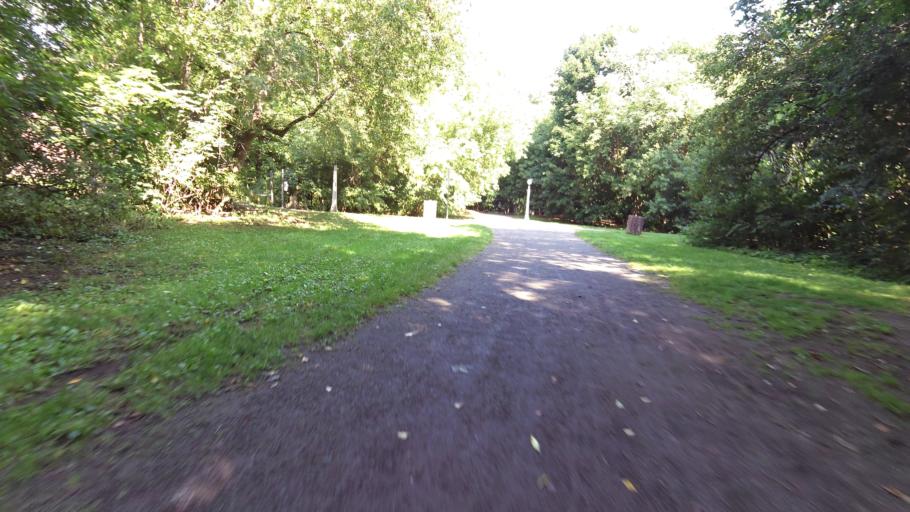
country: CA
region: Ontario
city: Ottawa
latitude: 45.3887
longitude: -75.7396
